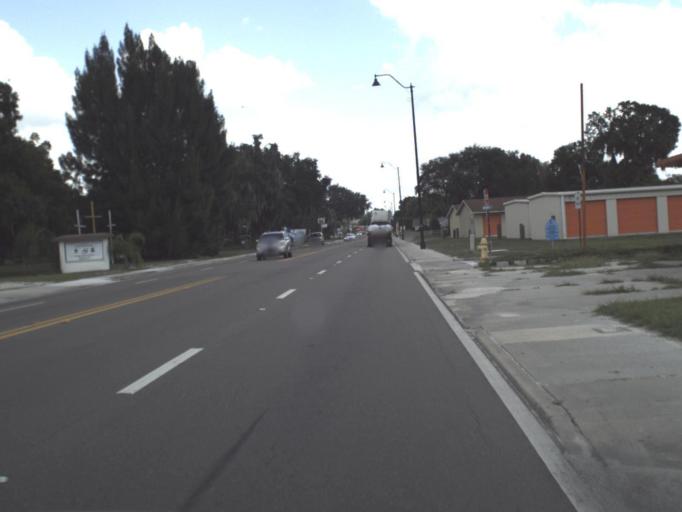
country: US
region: Florida
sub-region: Hardee County
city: Bowling Green
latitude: 27.6419
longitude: -81.8233
